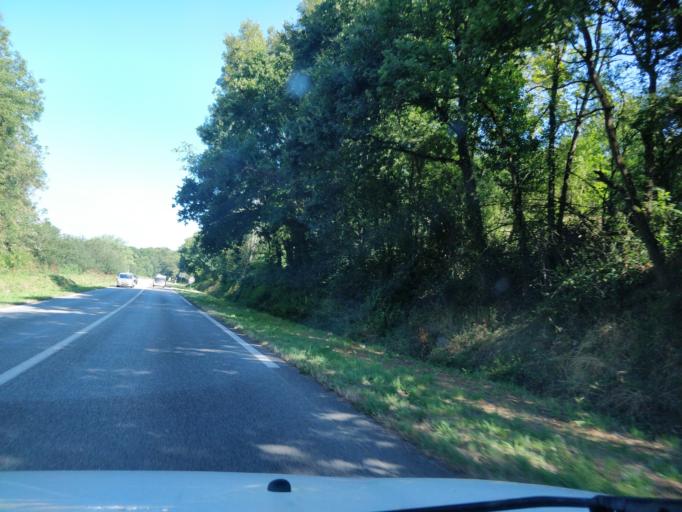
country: FR
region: Brittany
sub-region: Departement des Cotes-d'Armor
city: Pordic
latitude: 48.5813
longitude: -2.8237
